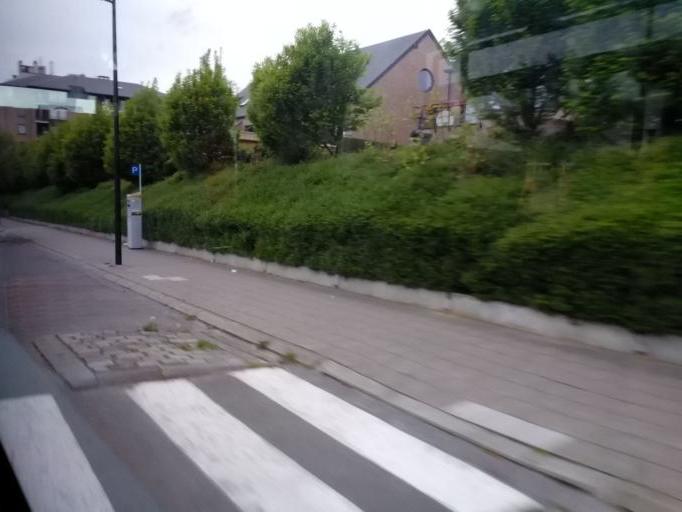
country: BE
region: Flanders
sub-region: Provincie Vlaams-Brabant
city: Diegem
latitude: 50.8591
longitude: 4.4064
